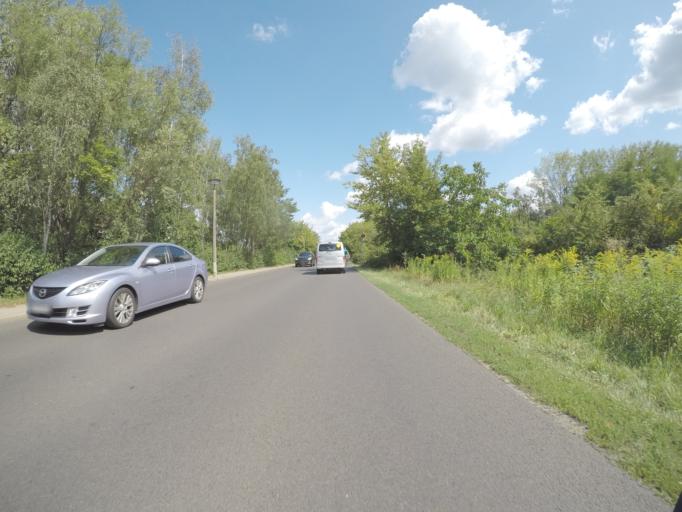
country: DE
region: Berlin
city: Kaulsdorf
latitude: 52.5027
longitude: 13.5895
